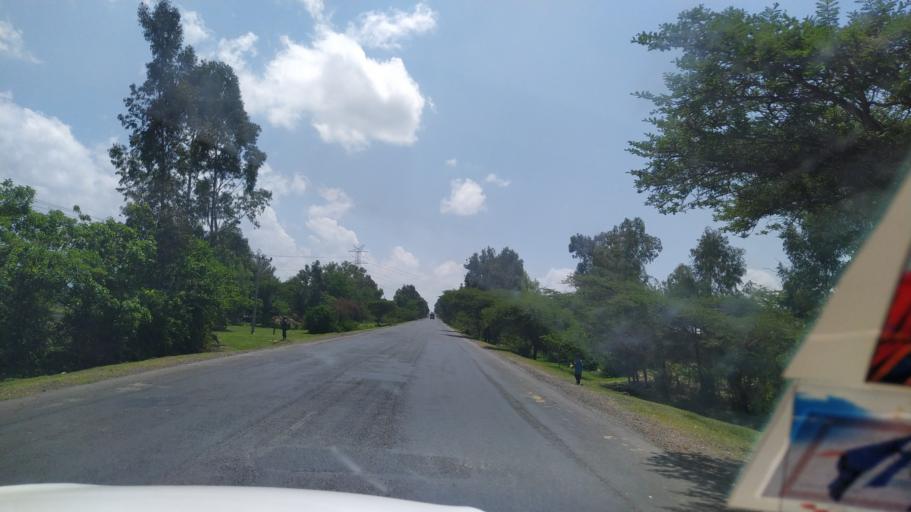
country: ET
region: Southern Nations, Nationalities, and People's Region
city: K'olito
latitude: 7.7506
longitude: 38.1279
